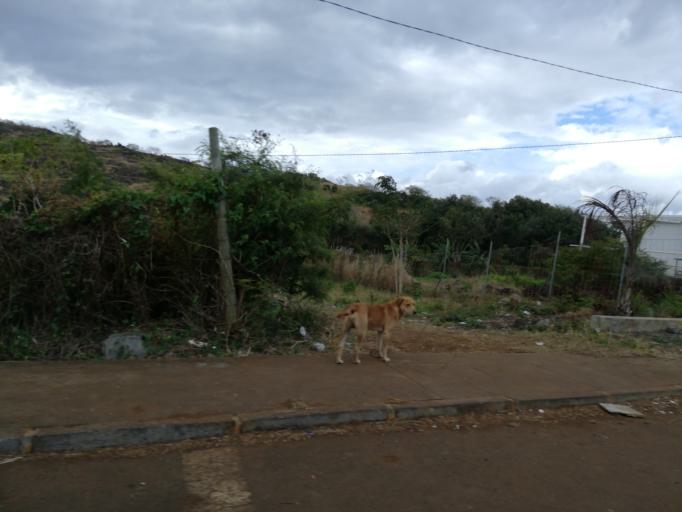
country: MU
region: Black River
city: Petite Riviere
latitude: -20.2104
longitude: 57.4644
